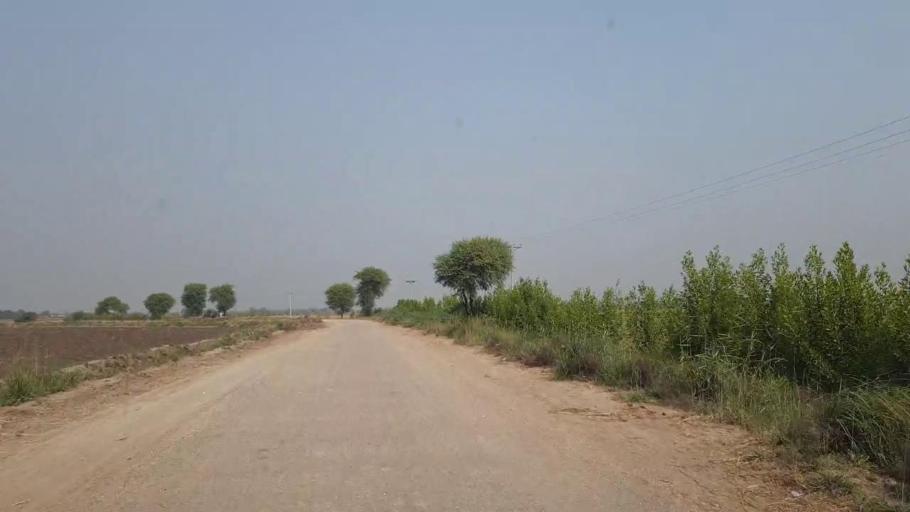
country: PK
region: Sindh
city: Matli
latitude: 25.1475
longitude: 68.7297
